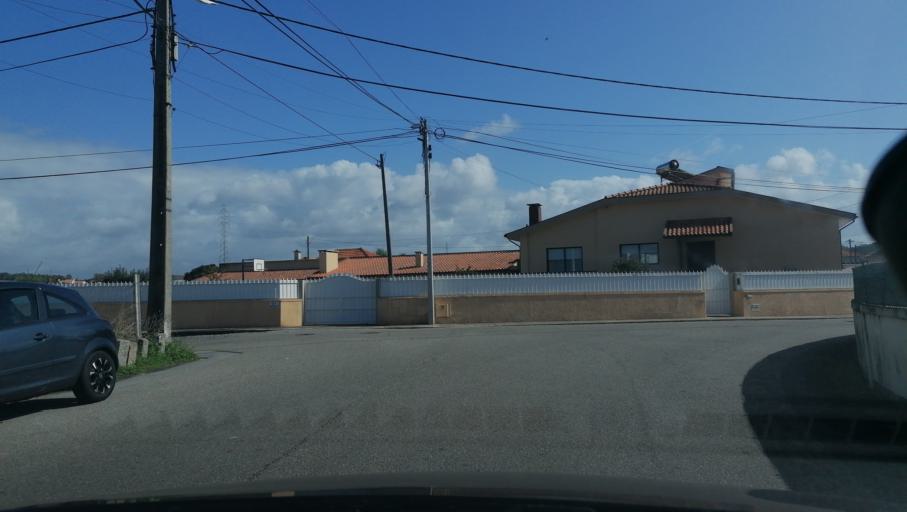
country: PT
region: Aveiro
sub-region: Espinho
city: Silvalde
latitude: 40.9902
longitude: -8.6367
